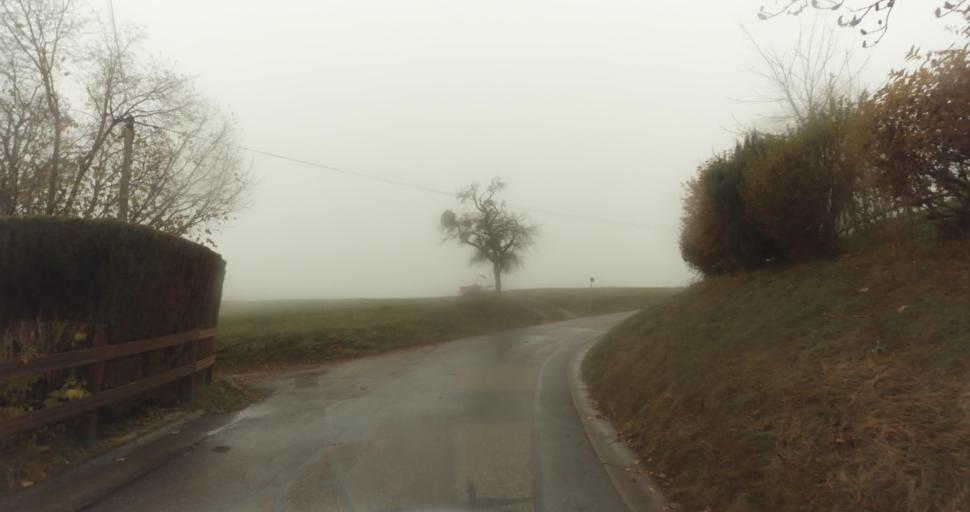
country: FR
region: Rhone-Alpes
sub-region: Departement de la Haute-Savoie
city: Villaz
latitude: 45.9700
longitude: 6.2022
